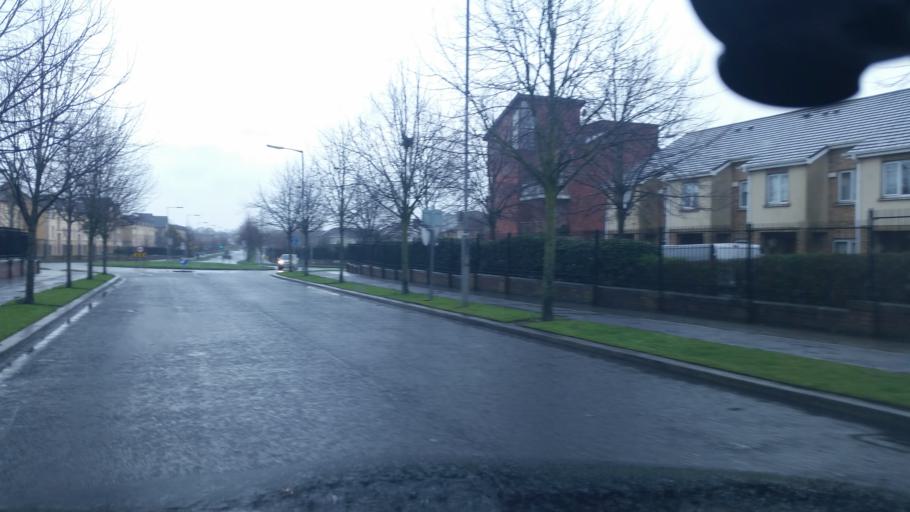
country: IE
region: Leinster
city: Hartstown
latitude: 53.3746
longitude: -6.4045
